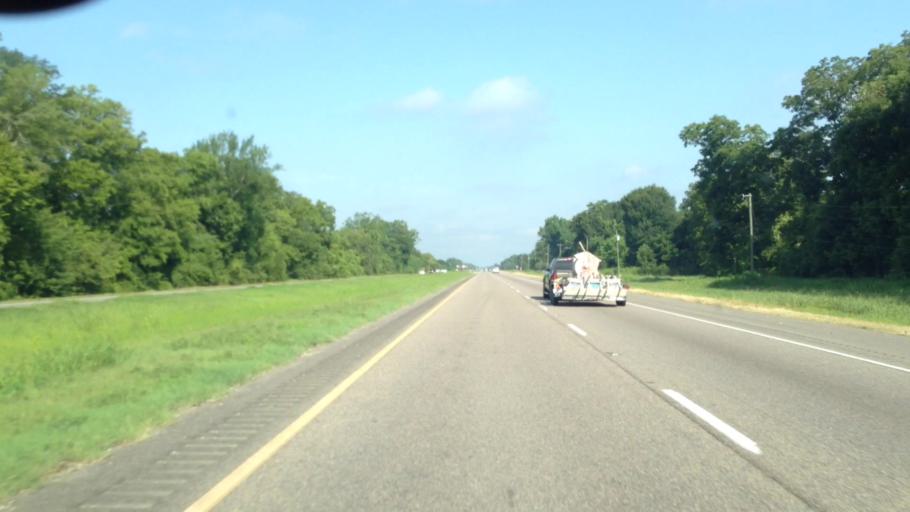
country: US
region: Louisiana
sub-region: West Baton Rouge Parish
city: Erwinville
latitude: 30.5112
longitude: -91.3422
